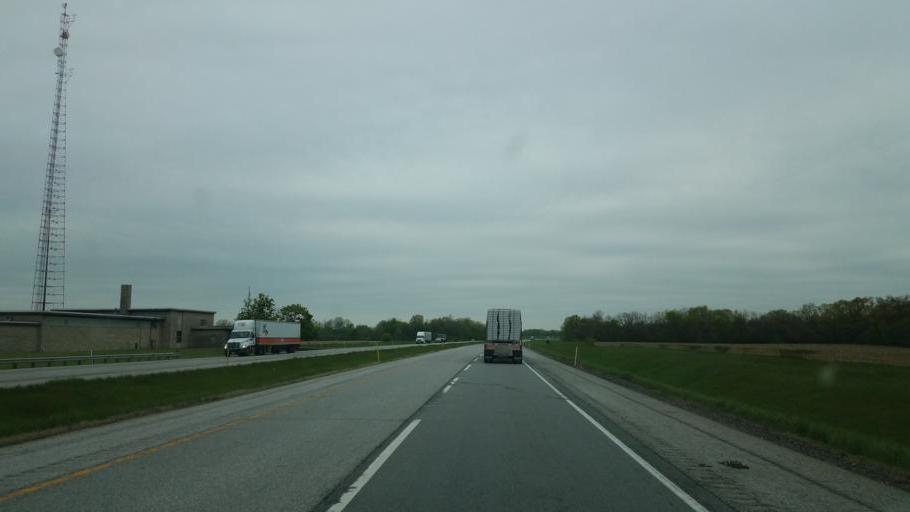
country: US
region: Michigan
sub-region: Saint Joseph County
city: White Pigeon
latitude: 41.7465
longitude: -85.5440
